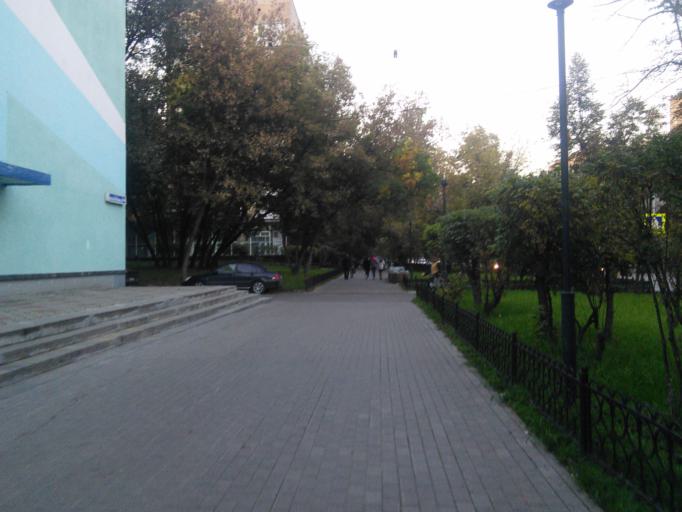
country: RU
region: Moscow
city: Novyye Cheremushki
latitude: 55.7122
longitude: 37.6062
